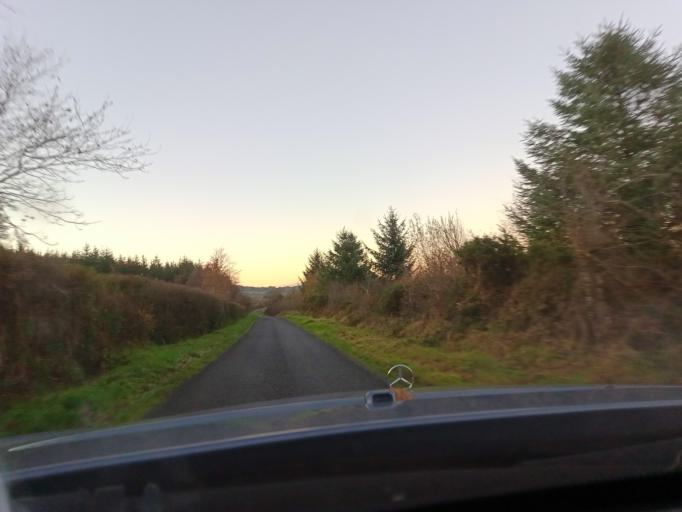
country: IE
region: Leinster
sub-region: Kilkenny
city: Thomastown
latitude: 52.4352
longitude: -7.1074
